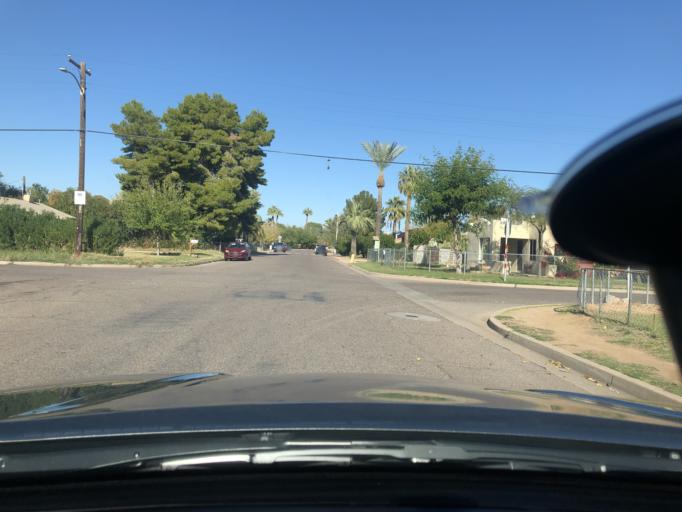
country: US
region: Arizona
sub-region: Maricopa County
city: Phoenix
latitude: 33.4715
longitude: -112.0266
